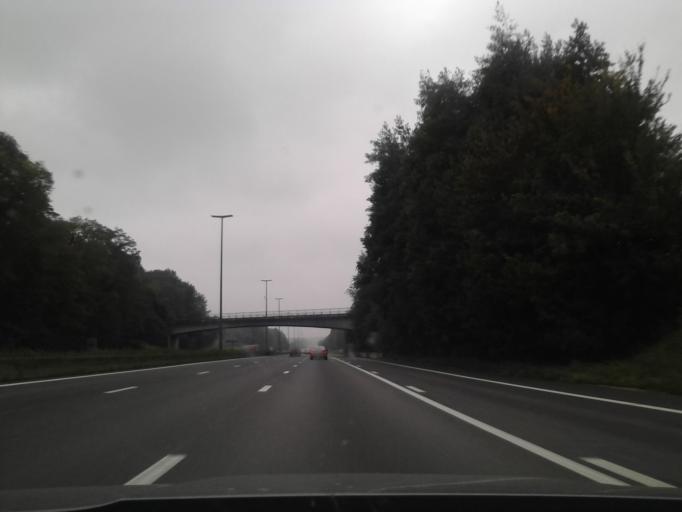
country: BE
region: Wallonia
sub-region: Province du Hainaut
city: Roeulx
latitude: 50.4834
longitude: 4.0371
